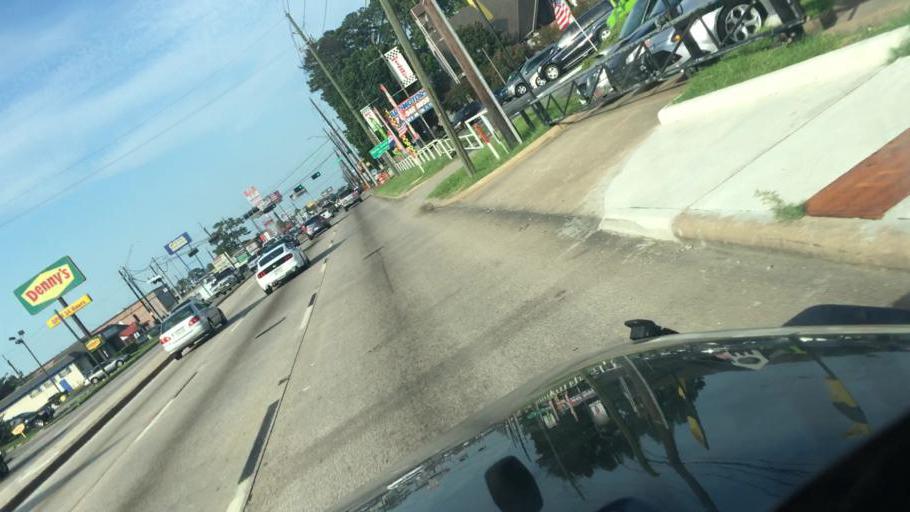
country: US
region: Texas
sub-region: Harris County
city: Spring
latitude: 30.0106
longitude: -95.4571
